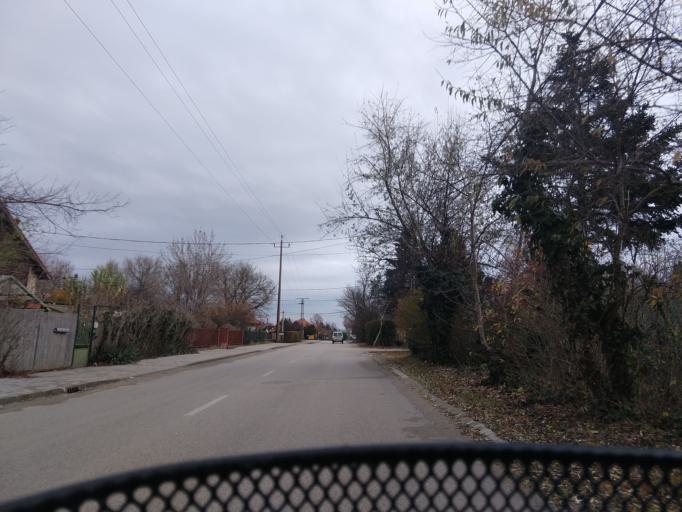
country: HU
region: Pest
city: Veresegyhaz
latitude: 47.6487
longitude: 19.2744
